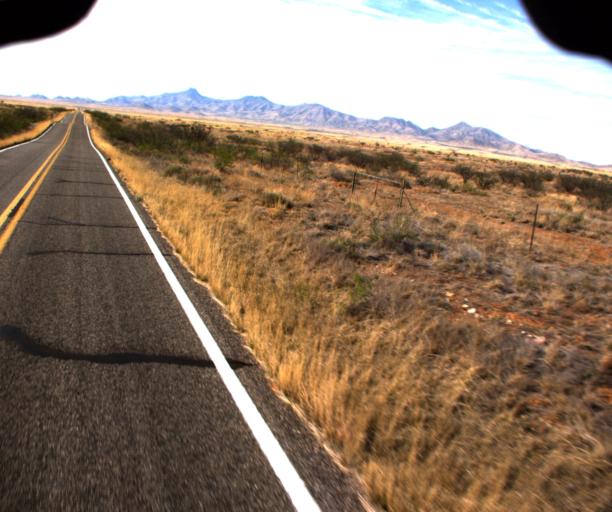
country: US
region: Arizona
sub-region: Cochise County
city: Willcox
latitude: 32.0518
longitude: -109.4927
